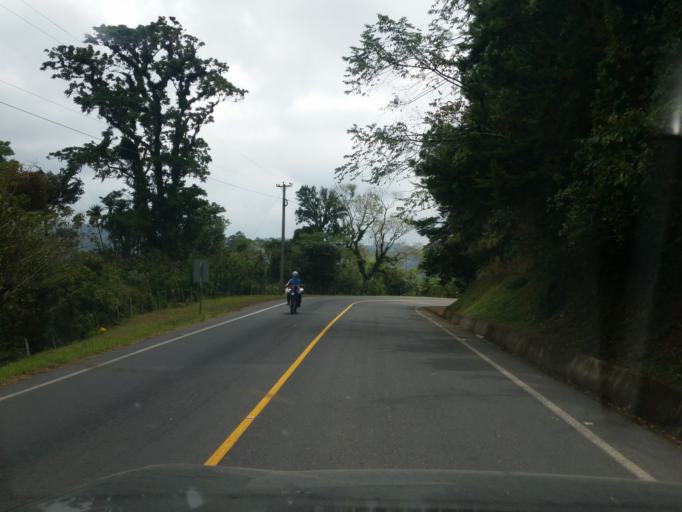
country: NI
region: Matagalpa
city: Matagalpa
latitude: 12.9940
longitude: -85.9218
